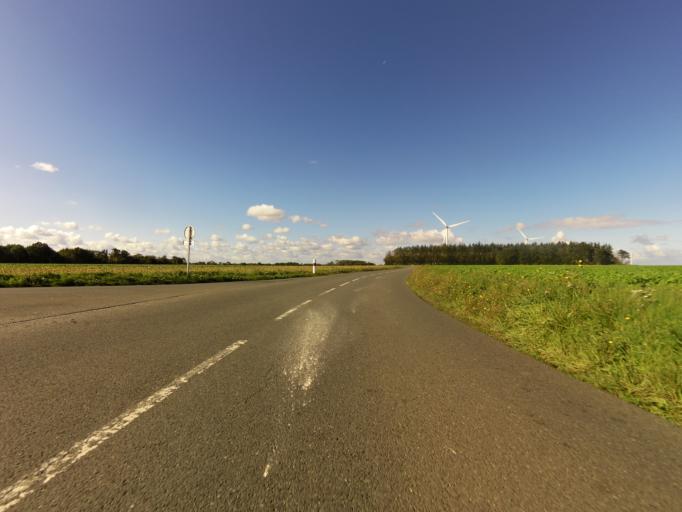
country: FR
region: Lower Normandy
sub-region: Departement du Calvados
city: Canon
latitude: 49.0458
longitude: -0.1420
